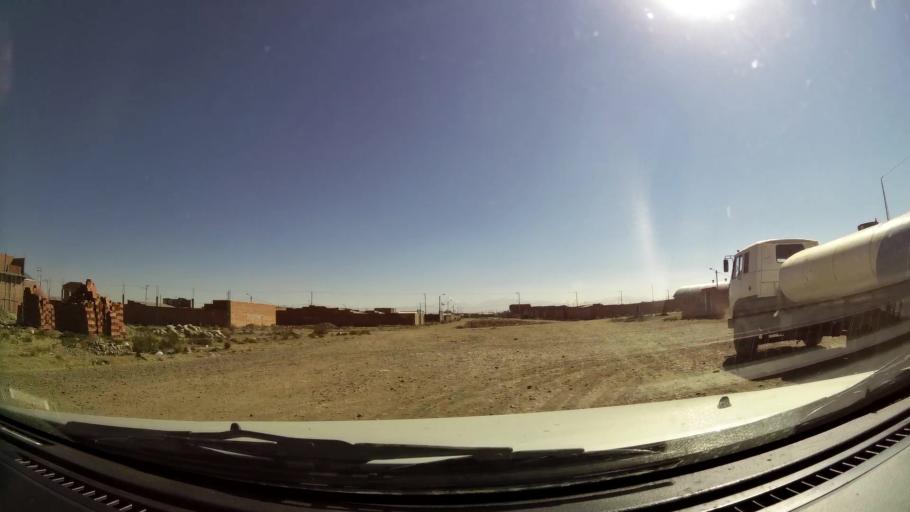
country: BO
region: La Paz
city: La Paz
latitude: -16.6253
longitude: -68.1955
